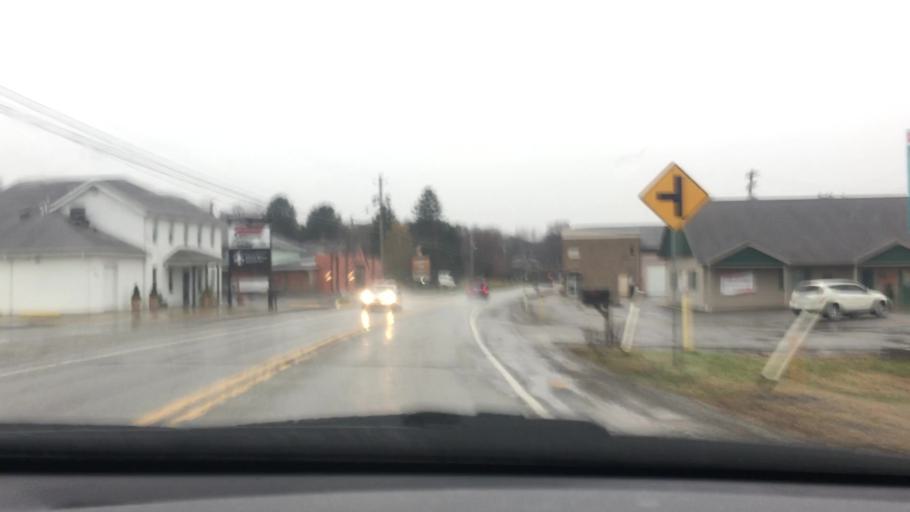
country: US
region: Pennsylvania
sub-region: Butler County
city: Saxonburg
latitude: 40.7170
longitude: -79.7537
